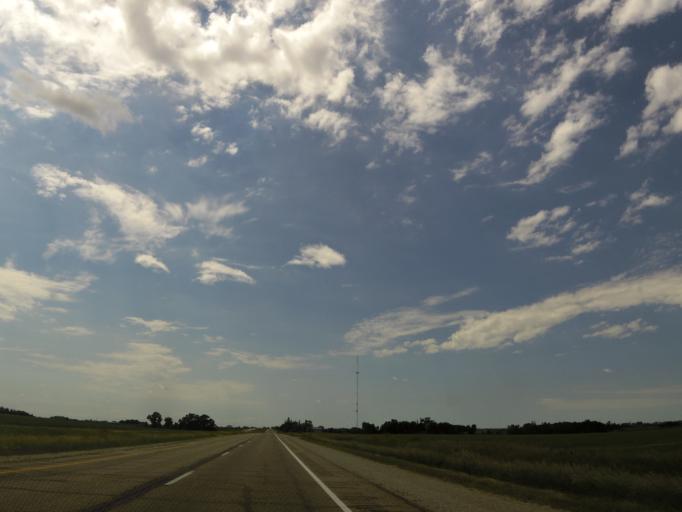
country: US
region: Iowa
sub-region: Bremer County
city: Tripoli
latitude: 42.7822
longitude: -92.3375
